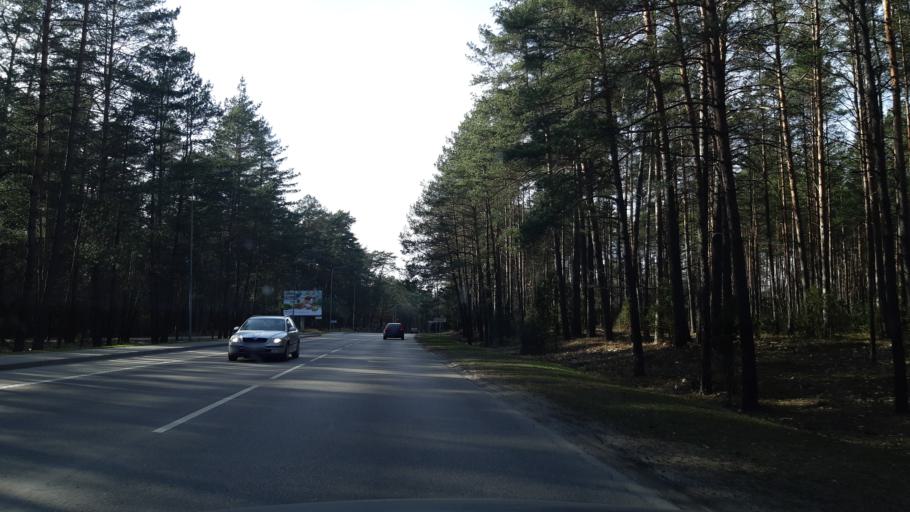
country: LT
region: Alytaus apskritis
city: Druskininkai
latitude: 54.0057
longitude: 24.0061
